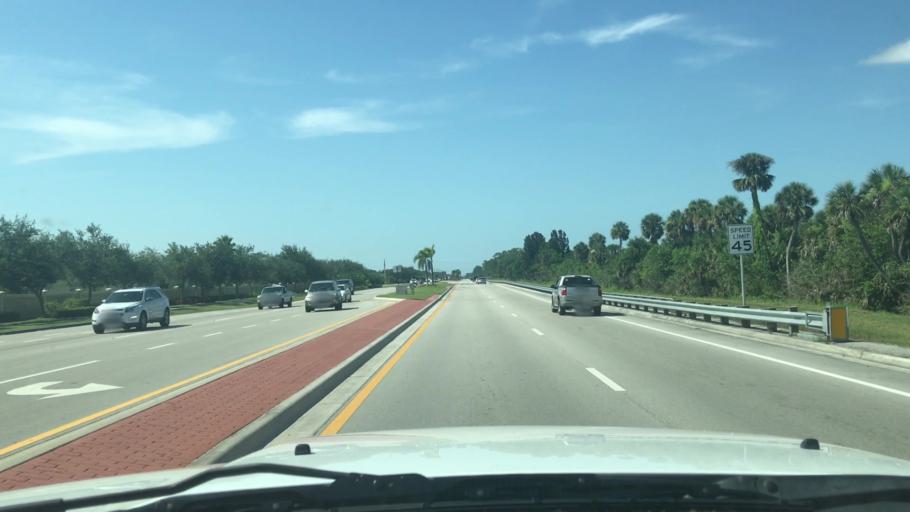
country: US
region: Florida
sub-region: Indian River County
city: West Vero Corridor
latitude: 27.6467
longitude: -80.4632
